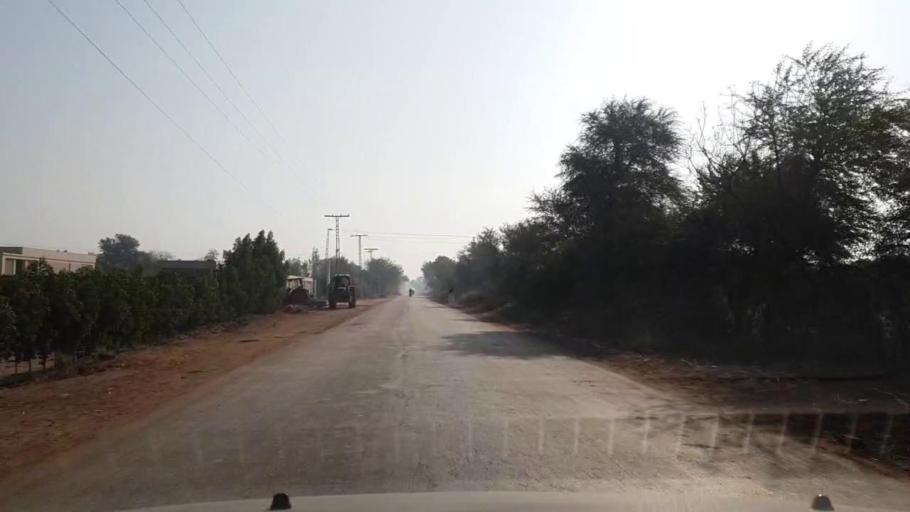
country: PK
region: Sindh
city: Matiari
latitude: 25.6004
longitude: 68.4534
